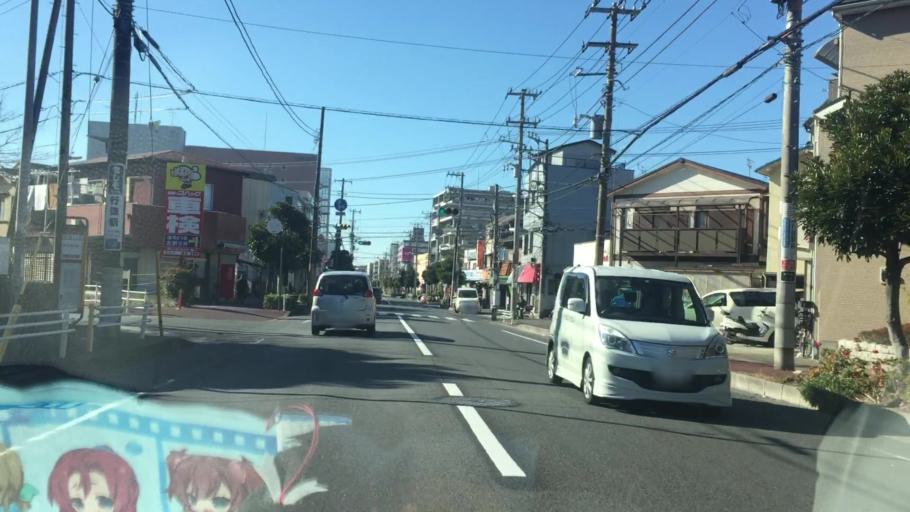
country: JP
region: Tokyo
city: Urayasu
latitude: 35.6697
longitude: 139.9082
